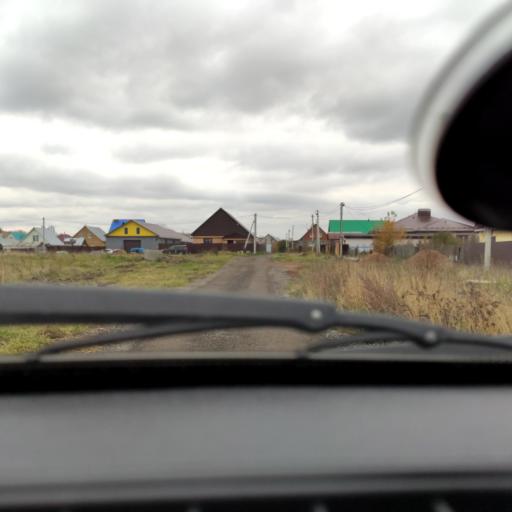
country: RU
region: Bashkortostan
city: Mikhaylovka
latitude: 54.7652
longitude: 55.9042
